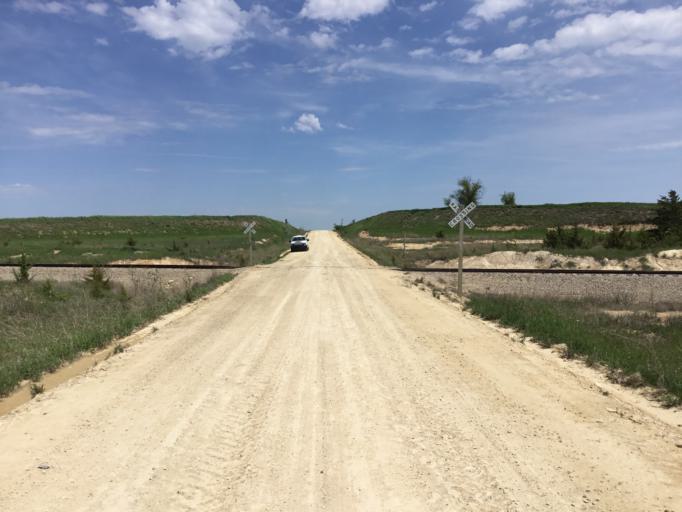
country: US
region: Kansas
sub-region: Mitchell County
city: Beloit
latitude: 39.5120
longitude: -98.3202
